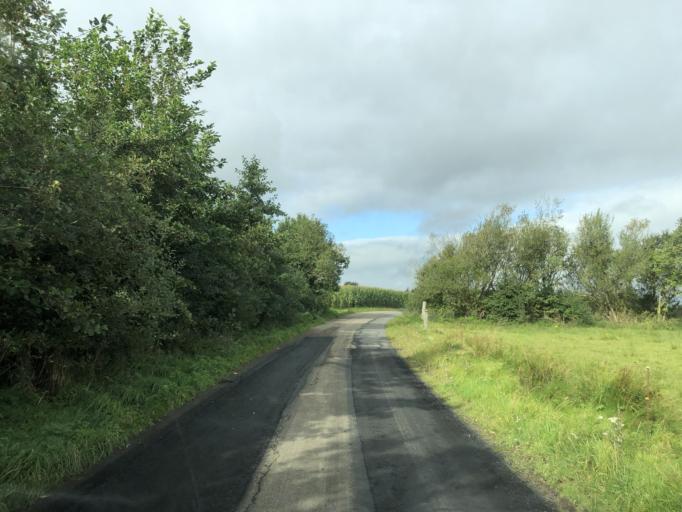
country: DK
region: Central Jutland
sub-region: Holstebro Kommune
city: Ulfborg
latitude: 56.3000
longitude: 8.4416
